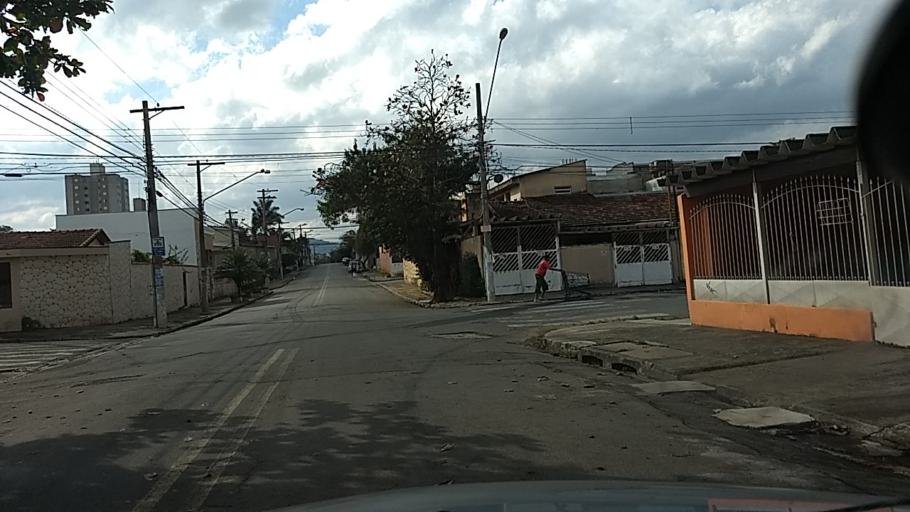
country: BR
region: Sao Paulo
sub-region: Carapicuiba
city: Carapicuiba
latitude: -23.5289
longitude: -46.8140
